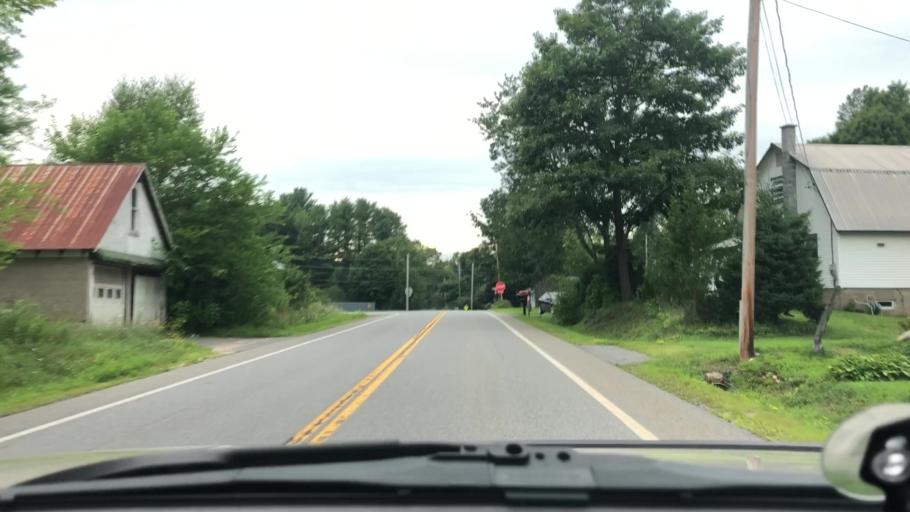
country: US
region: New York
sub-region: Saratoga County
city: Corinth
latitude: 43.2121
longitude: -73.7971
